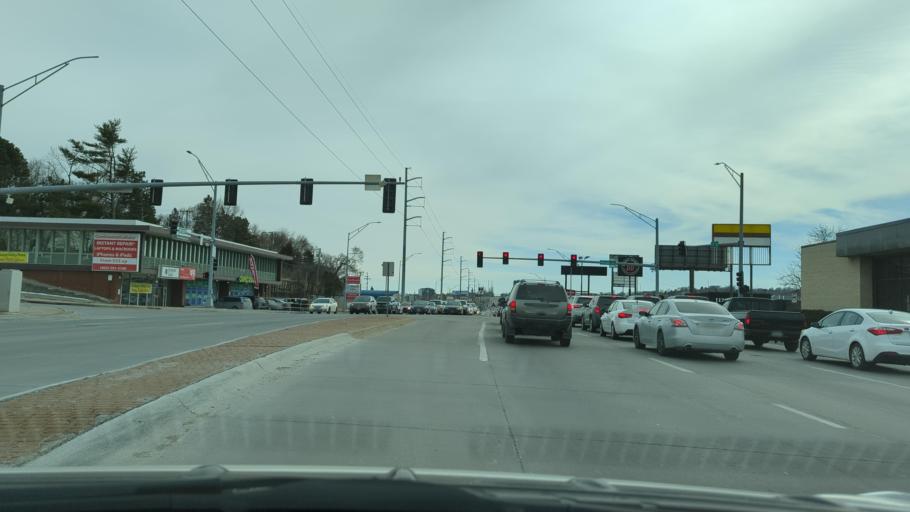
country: US
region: Nebraska
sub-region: Douglas County
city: Ralston
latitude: 41.2585
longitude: -96.0239
